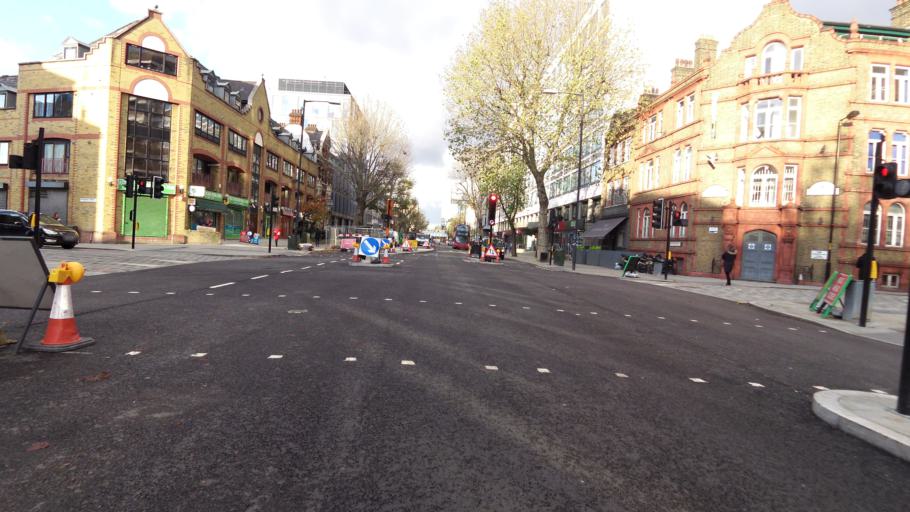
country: GB
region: England
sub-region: Greater London
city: Lambeth
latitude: 51.5007
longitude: -0.1047
